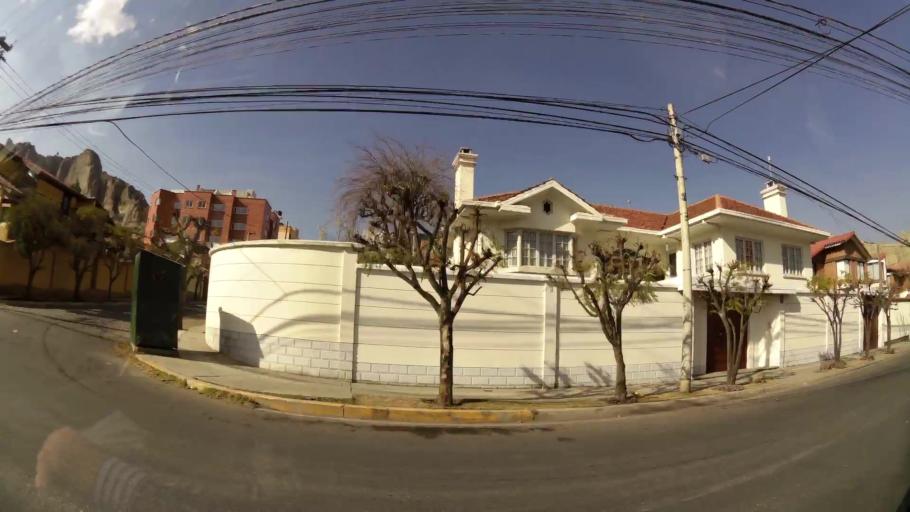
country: BO
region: La Paz
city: La Paz
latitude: -16.5269
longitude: -68.0722
